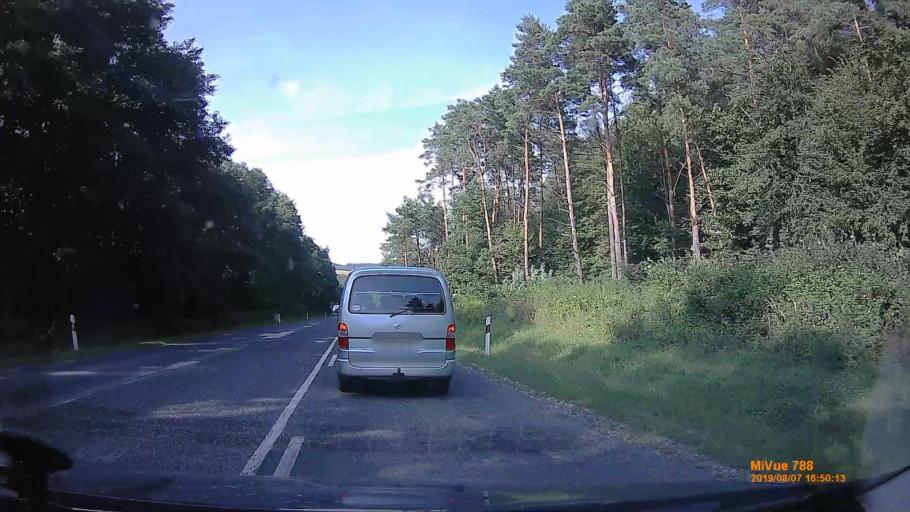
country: HU
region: Zala
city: Lenti
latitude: 46.6812
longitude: 16.6710
